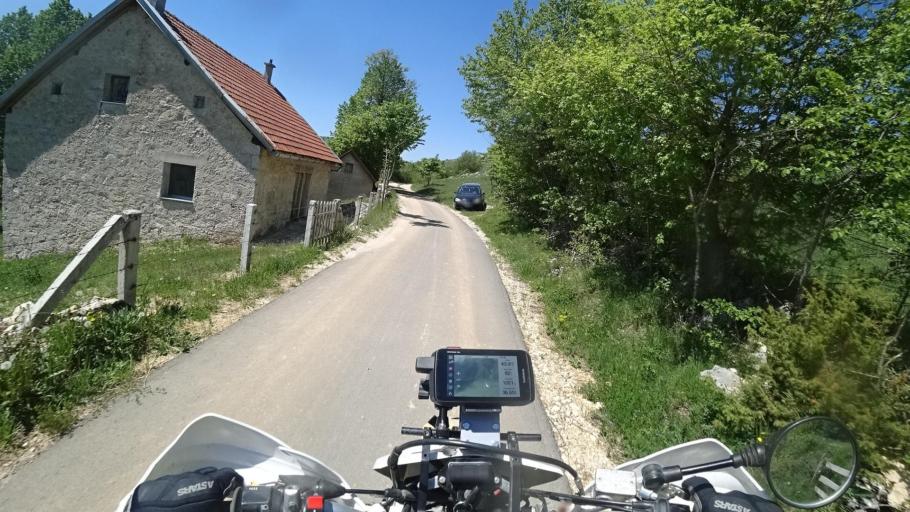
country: BA
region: Federation of Bosnia and Herzegovina
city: Rumboci
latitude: 43.8321
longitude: 17.4443
